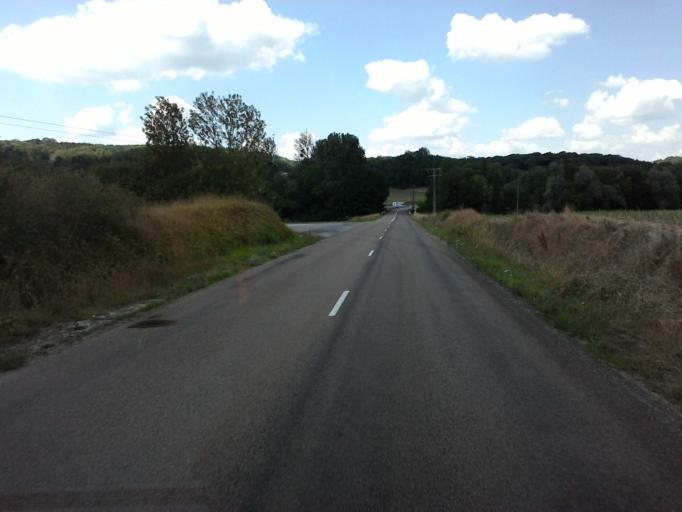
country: FR
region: Franche-Comte
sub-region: Departement du Jura
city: Montmorot
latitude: 46.7673
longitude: 5.5579
